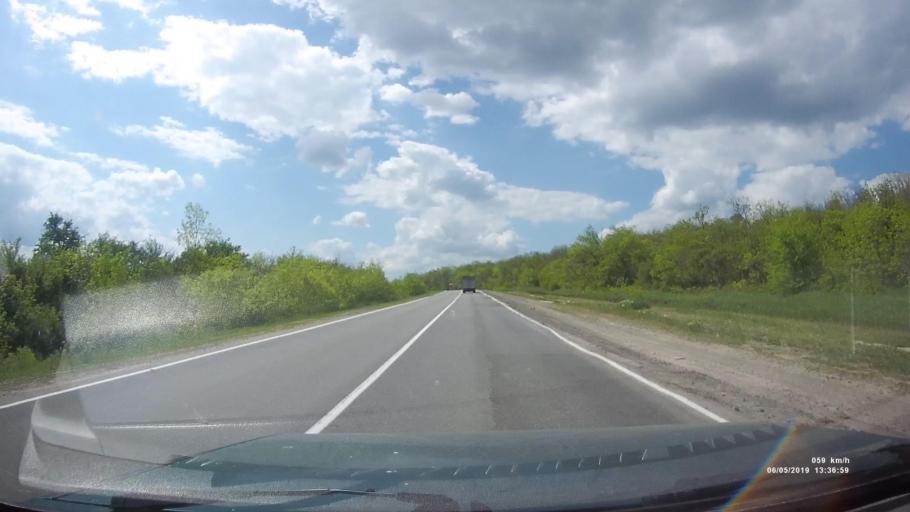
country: RU
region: Rostov
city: Ust'-Donetskiy
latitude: 47.6896
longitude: 40.7232
